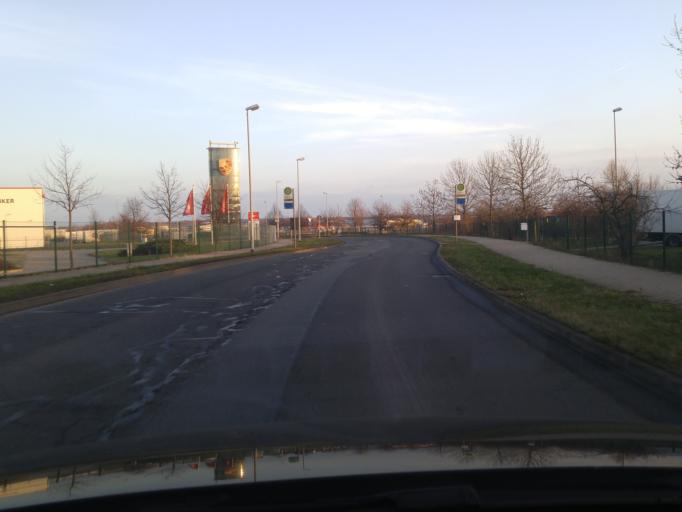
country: DE
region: Saxony
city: Zwochau
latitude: 51.4138
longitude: 12.2929
